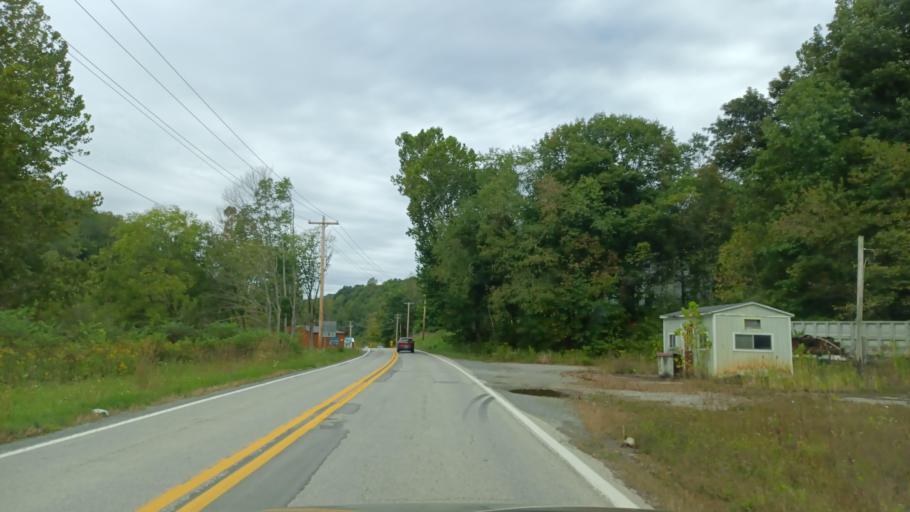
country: US
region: West Virginia
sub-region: Taylor County
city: Grafton
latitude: 39.3336
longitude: -79.8493
